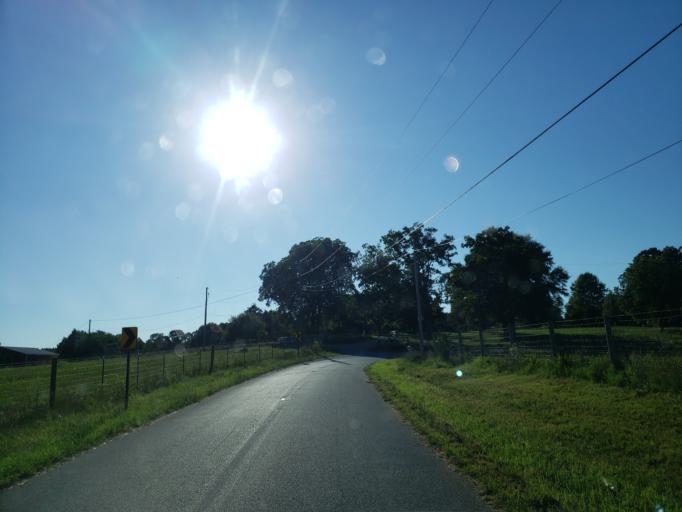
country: US
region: Georgia
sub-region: Bartow County
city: Euharlee
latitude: 34.1118
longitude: -84.9916
